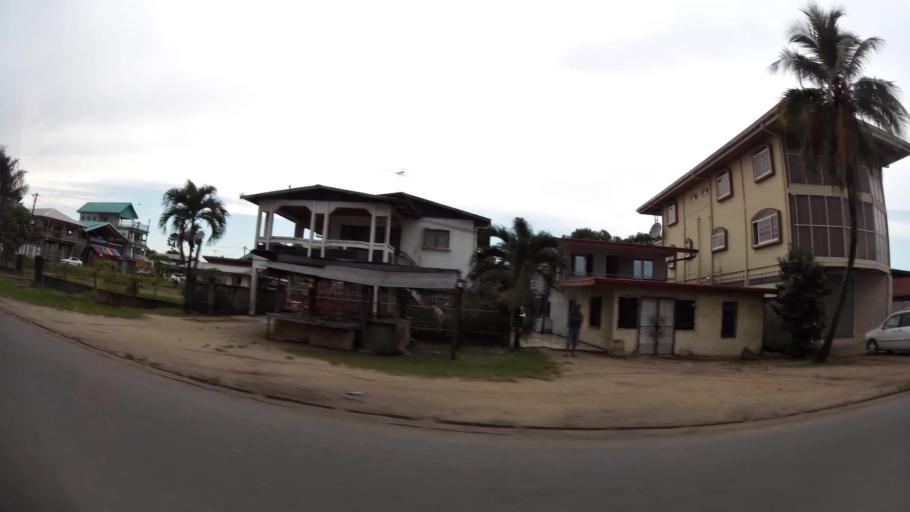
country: SR
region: Paramaribo
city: Paramaribo
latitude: 5.8040
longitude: -55.1773
